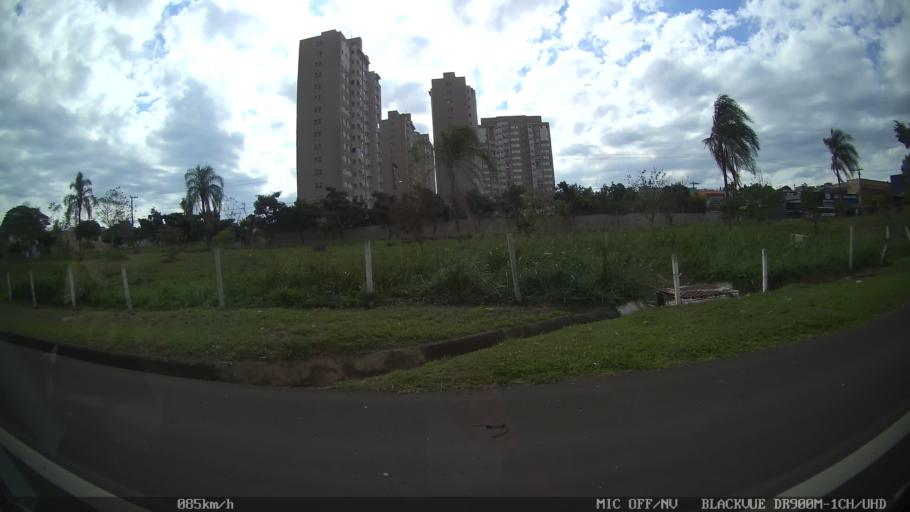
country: BR
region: Sao Paulo
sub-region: Limeira
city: Limeira
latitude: -22.5654
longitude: -47.4326
